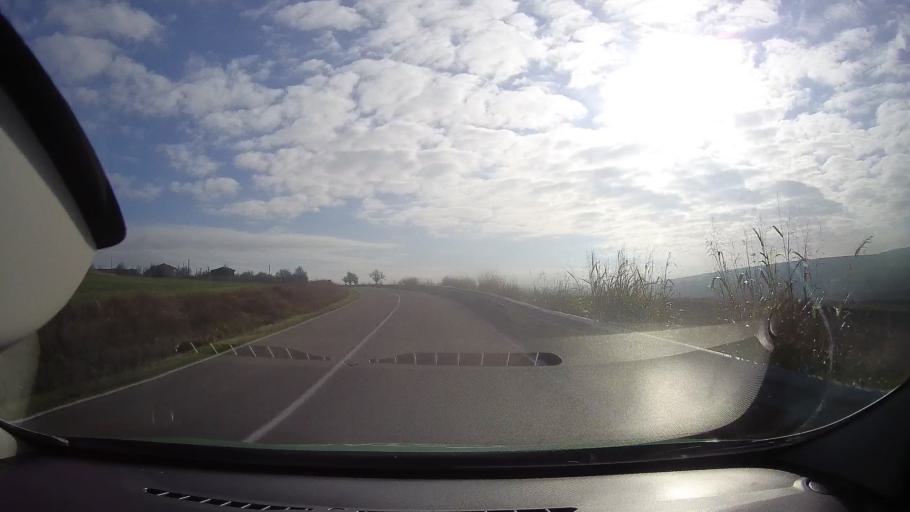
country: RO
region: Tulcea
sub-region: Comuna Bestepe
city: Bestepe
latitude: 45.0822
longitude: 29.0243
